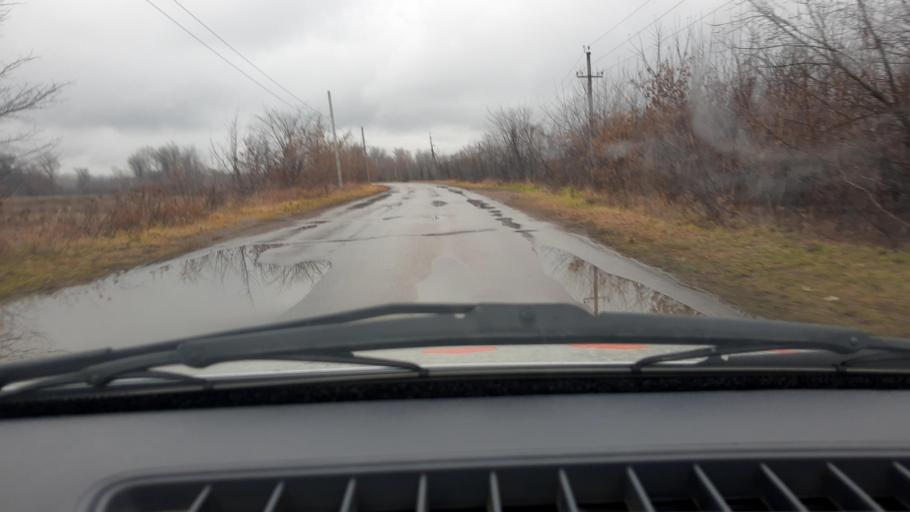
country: RU
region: Bashkortostan
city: Iglino
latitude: 54.8028
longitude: 56.1951
